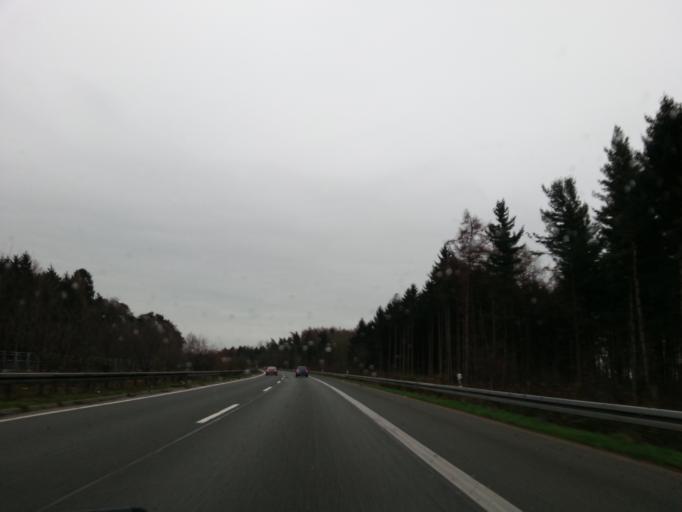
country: DE
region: North Rhine-Westphalia
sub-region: Regierungsbezirk Dusseldorf
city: Mehrhoog
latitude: 51.7859
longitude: 6.5006
